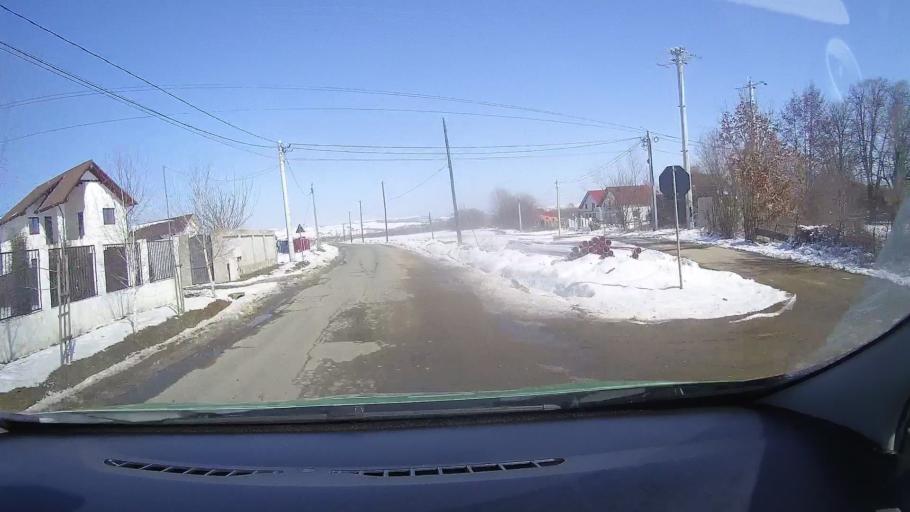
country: RO
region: Brasov
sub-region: Comuna Mandra
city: Mandra
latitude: 45.8257
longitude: 25.0095
